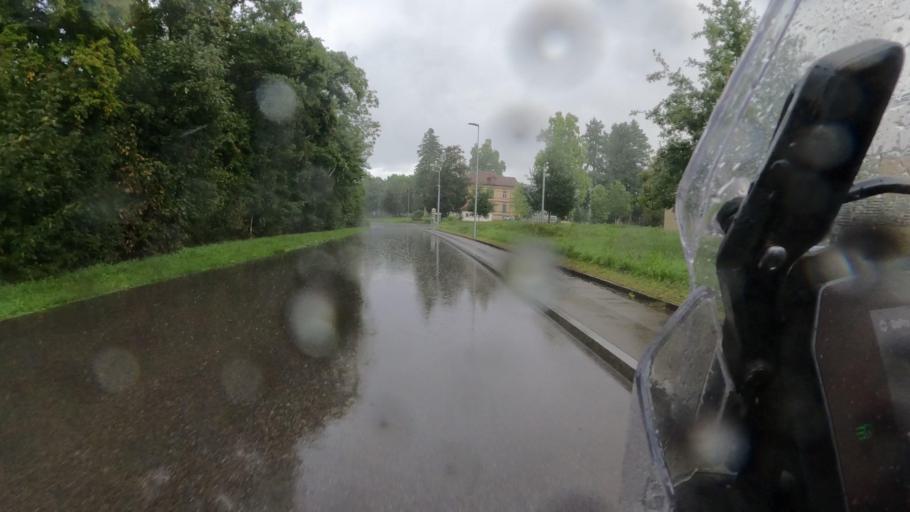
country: CH
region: Zurich
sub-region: Bezirk Andelfingen
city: Dachsen
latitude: 47.6362
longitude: 8.6054
